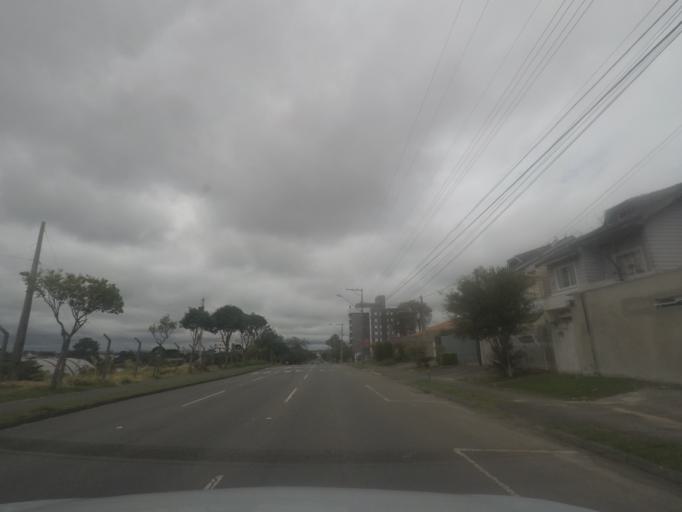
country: BR
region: Parana
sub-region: Pinhais
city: Pinhais
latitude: -25.4417
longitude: -49.2290
